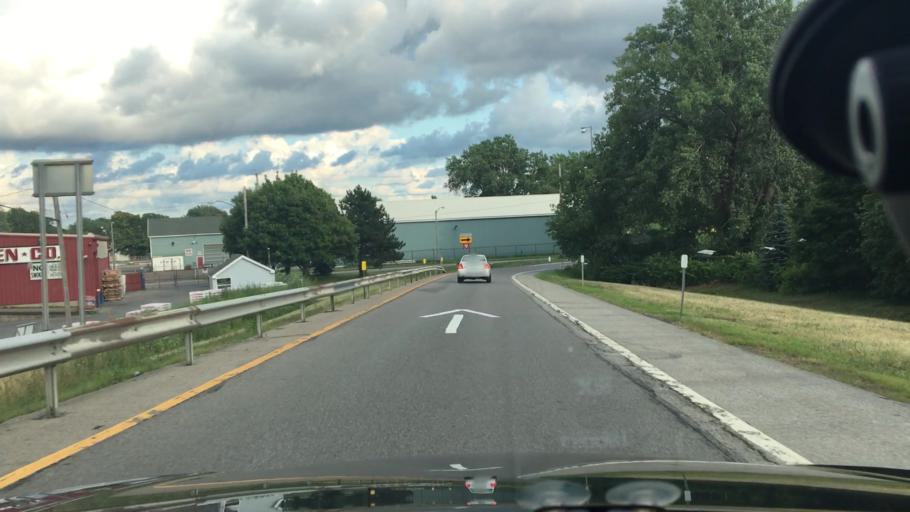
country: US
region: New York
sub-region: Erie County
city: West Seneca
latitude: 42.8670
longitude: -78.8277
